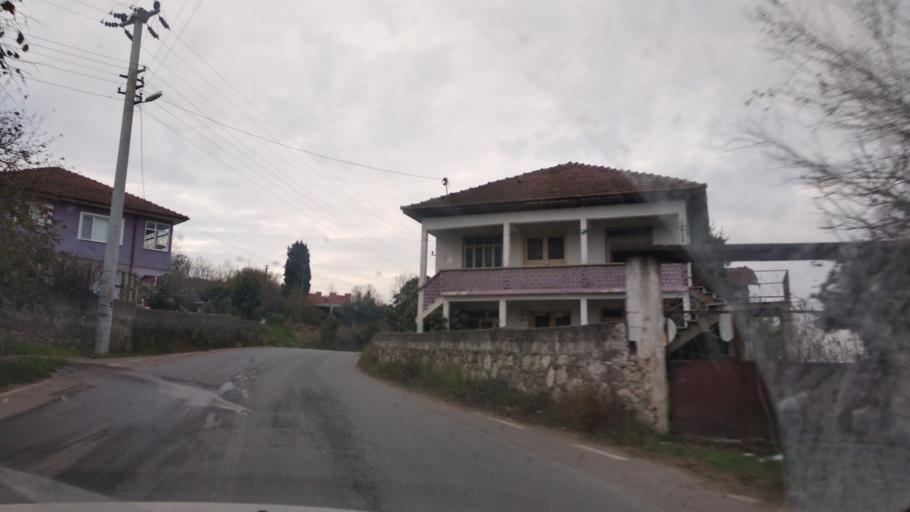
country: TR
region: Sakarya
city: Ortakoy
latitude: 41.0392
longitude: 30.6429
